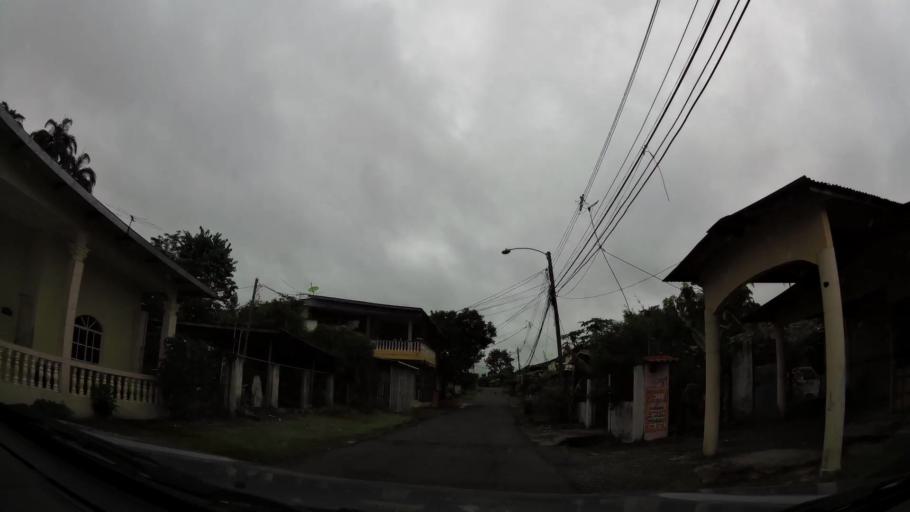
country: PA
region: Chiriqui
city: La Concepcion
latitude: 8.5186
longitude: -82.6166
